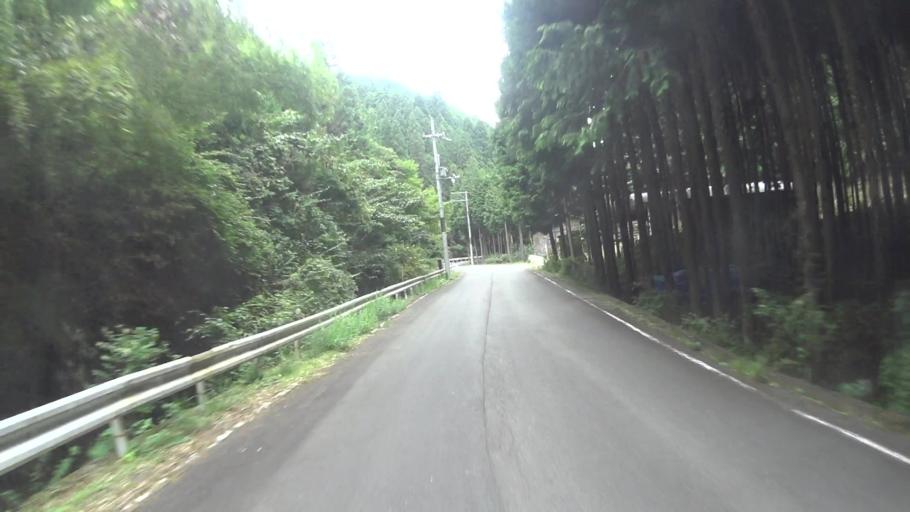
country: JP
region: Kyoto
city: Uji
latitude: 34.8092
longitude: 135.8717
